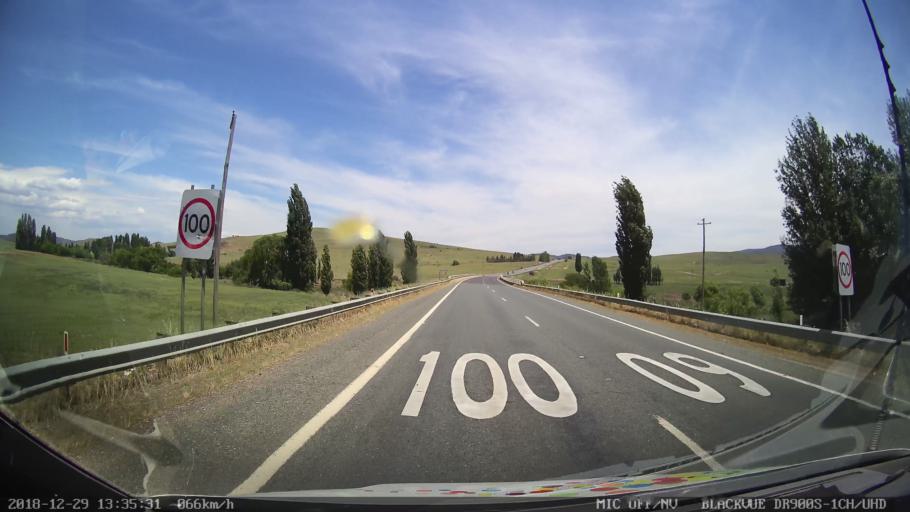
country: AU
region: New South Wales
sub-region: Cooma-Monaro
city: Cooma
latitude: -35.9603
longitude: 149.1493
